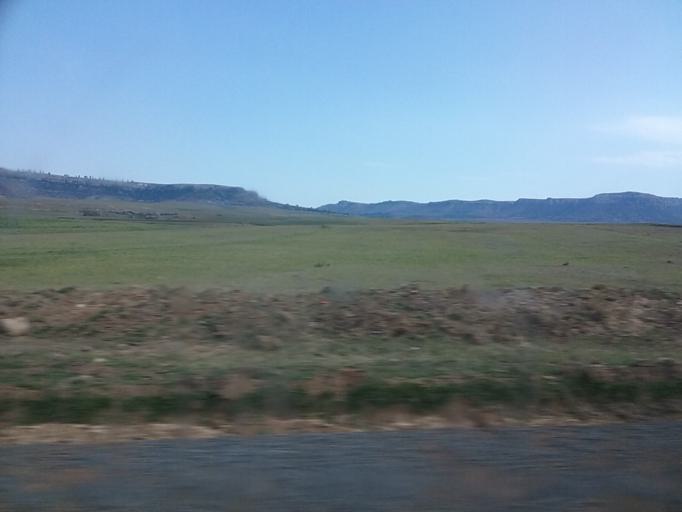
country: LS
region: Berea
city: Teyateyaneng
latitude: -29.0840
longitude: 27.8995
